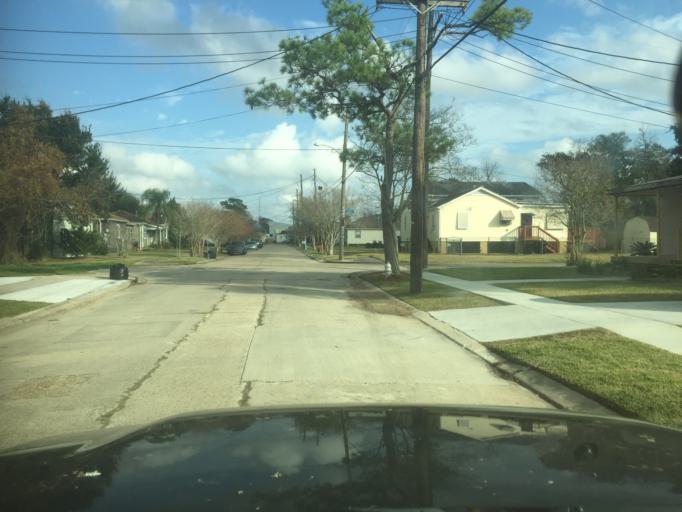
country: US
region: Louisiana
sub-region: Orleans Parish
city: New Orleans
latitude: 29.9899
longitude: -90.0828
